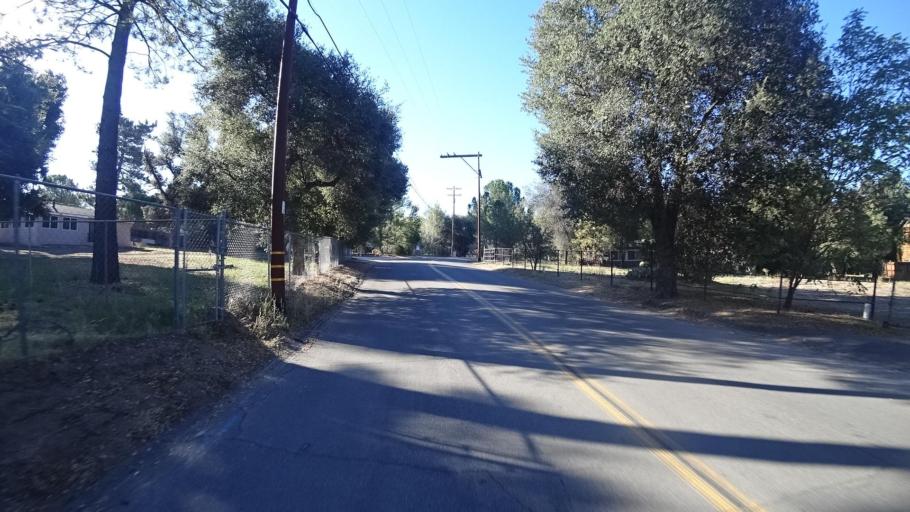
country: US
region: California
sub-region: San Diego County
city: Pine Valley
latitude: 32.8213
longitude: -116.5250
